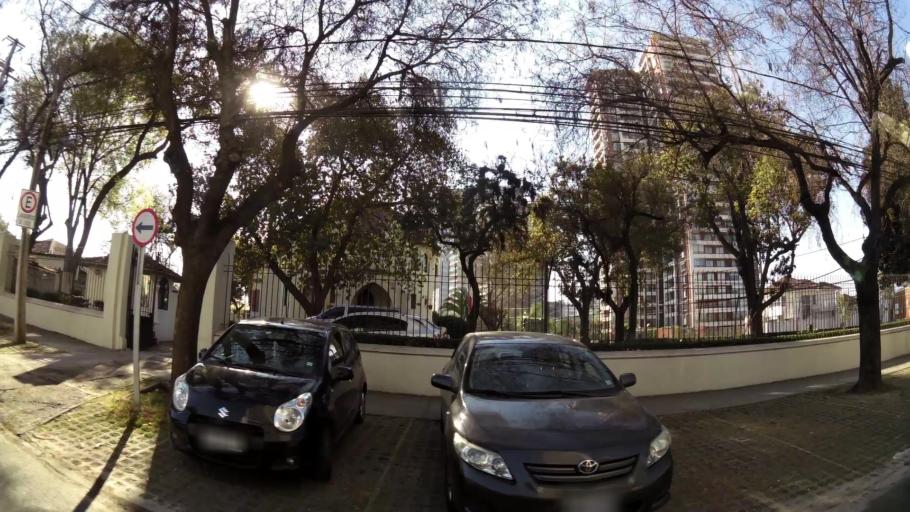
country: CL
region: Santiago Metropolitan
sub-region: Provincia de Santiago
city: Villa Presidente Frei, Nunoa, Santiago, Chile
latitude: -33.4551
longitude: -70.5858
